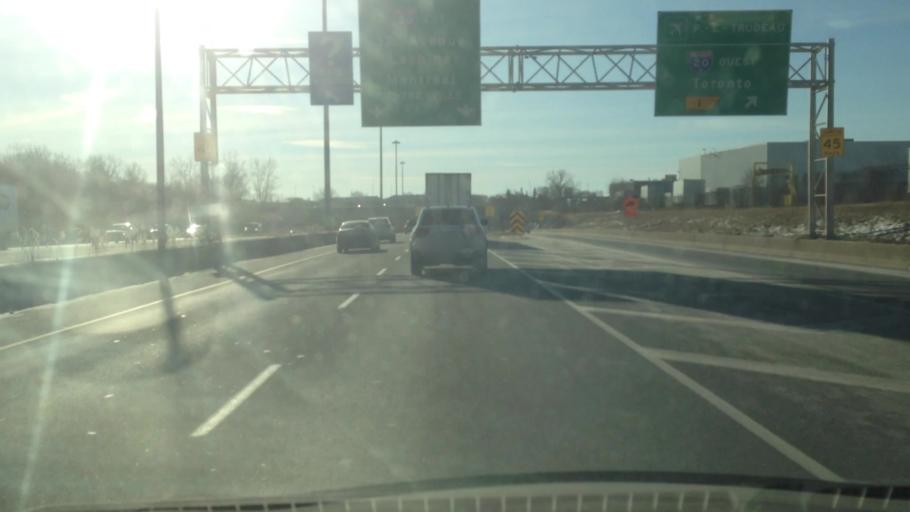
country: CA
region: Quebec
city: Cote-Saint-Luc
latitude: 45.4528
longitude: -73.6973
